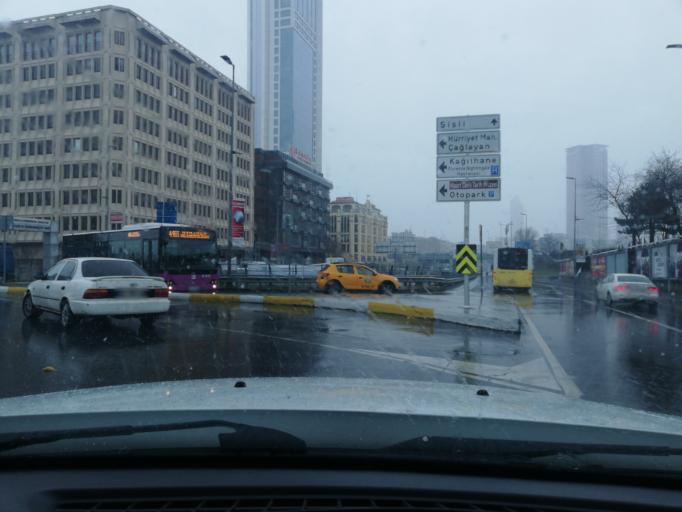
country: TR
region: Istanbul
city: Sisli
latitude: 41.0685
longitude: 28.9833
